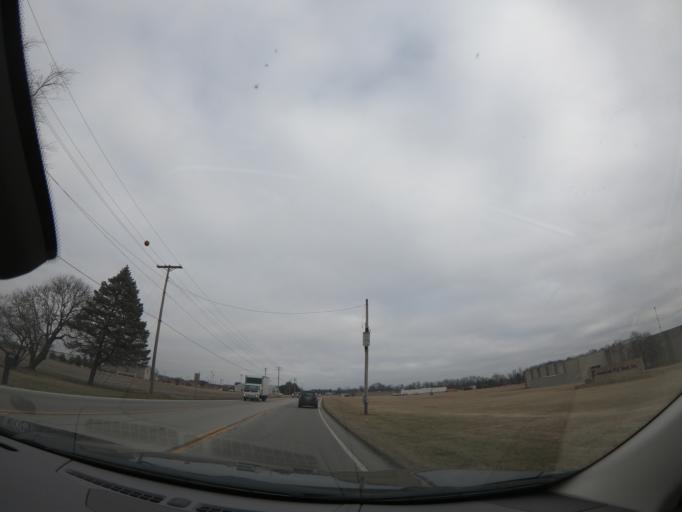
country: US
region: Kentucky
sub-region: Nelson County
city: Bardstown
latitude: 37.8268
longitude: -85.4310
